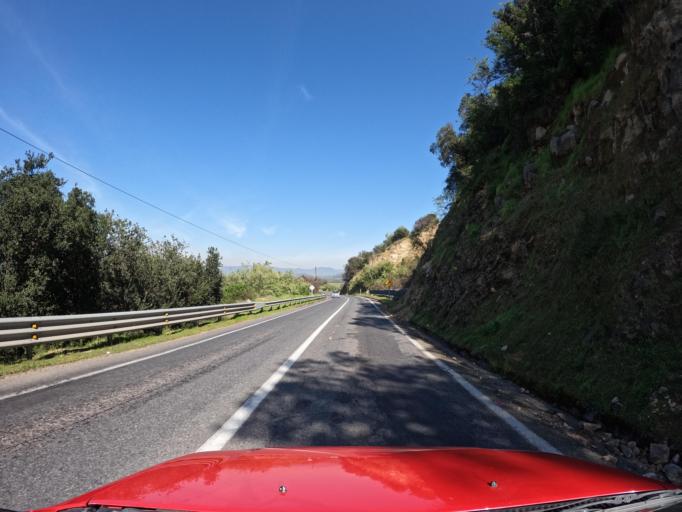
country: CL
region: Maule
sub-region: Provincia de Curico
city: Rauco
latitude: -35.0487
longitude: -71.5937
